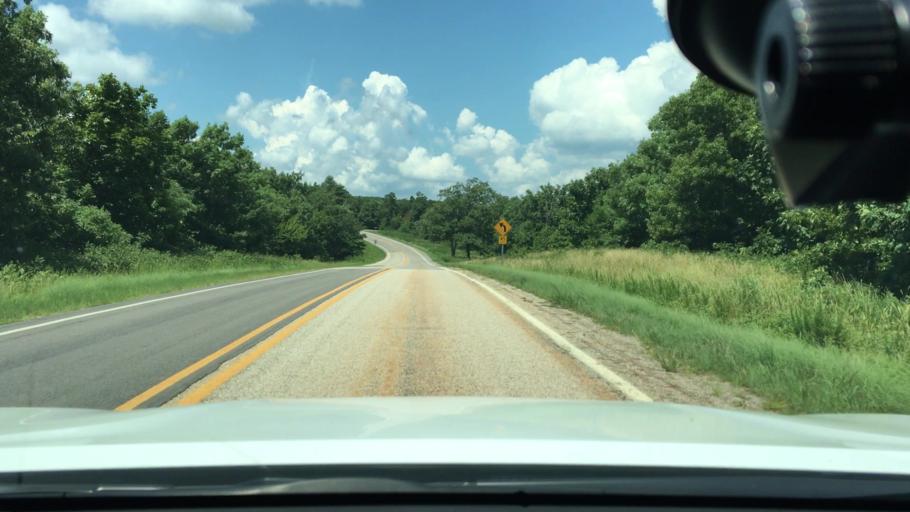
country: US
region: Arkansas
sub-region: Logan County
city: Paris
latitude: 35.1767
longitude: -93.6127
